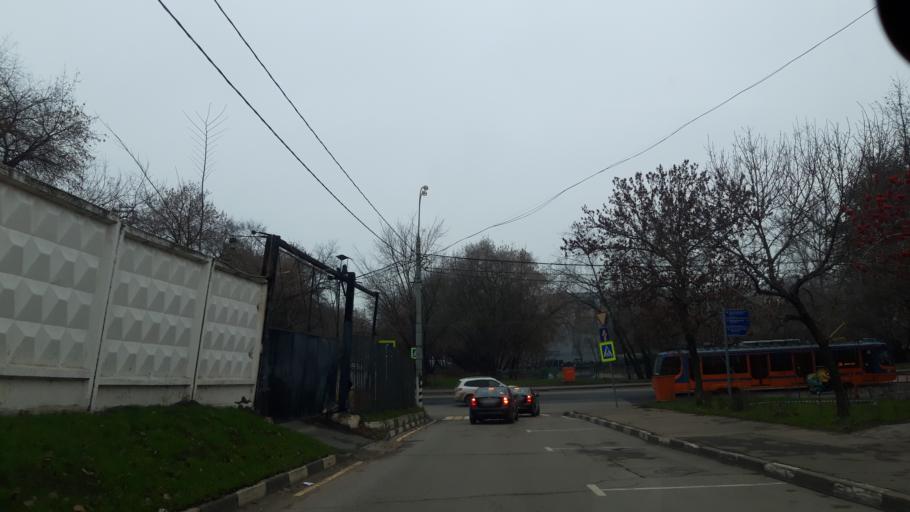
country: RU
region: Moscow
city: Taganskiy
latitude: 55.7497
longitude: 37.6772
